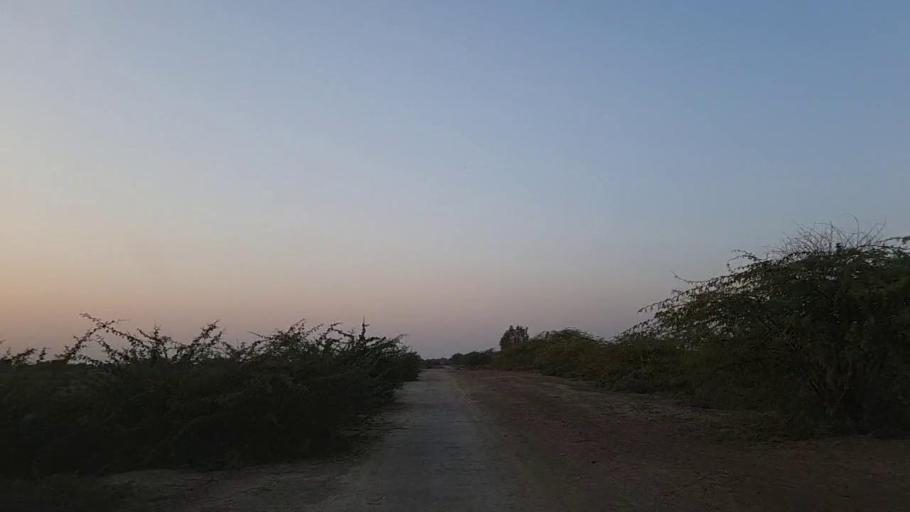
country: PK
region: Sindh
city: Naukot
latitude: 24.8854
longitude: 69.3704
